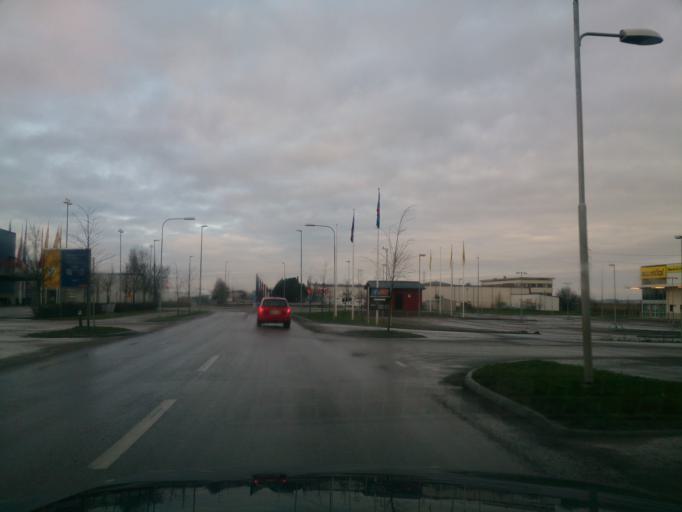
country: SE
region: OEstergoetland
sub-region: Linkopings Kommun
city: Linkoping
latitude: 58.4336
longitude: 15.6003
